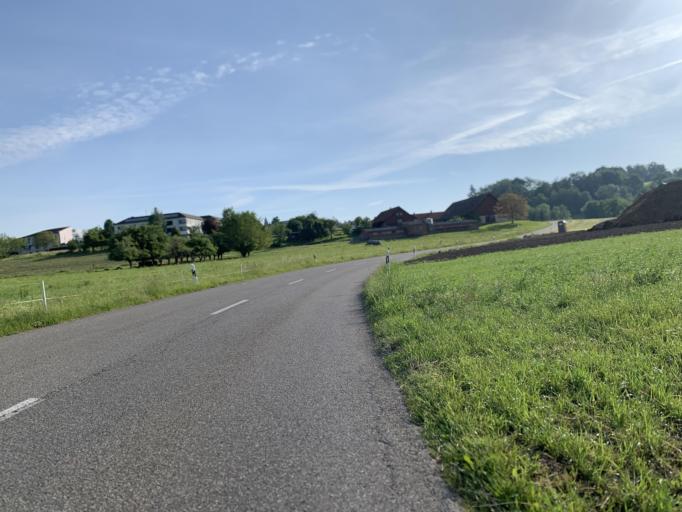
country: CH
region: Zurich
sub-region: Bezirk Uster
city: Uster / Kirch-Uster
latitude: 47.3349
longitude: 8.7152
